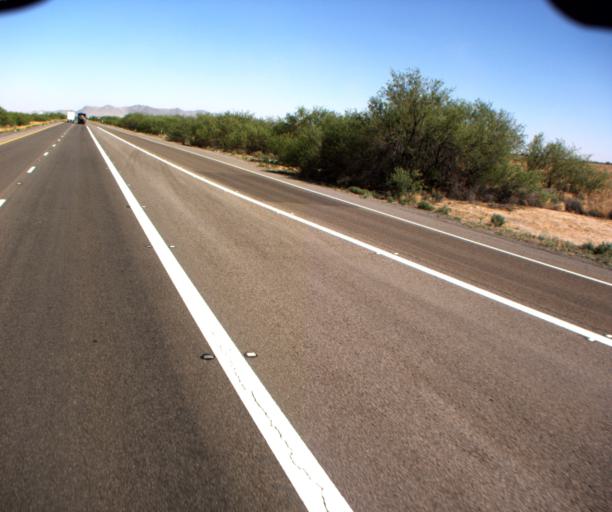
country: US
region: Arizona
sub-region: Pinal County
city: Casa Grande
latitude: 32.8279
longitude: -111.8215
